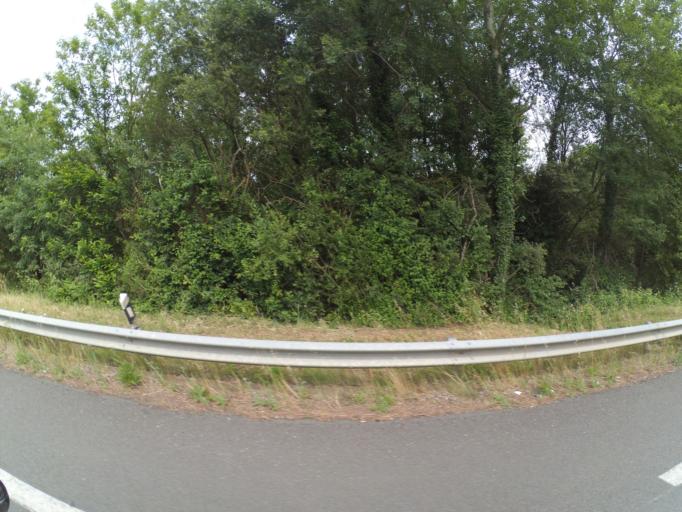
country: FR
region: Pays de la Loire
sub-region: Departement de la Vendee
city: Saint-Georges-de-Montaigu
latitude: 46.9360
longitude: -1.2899
